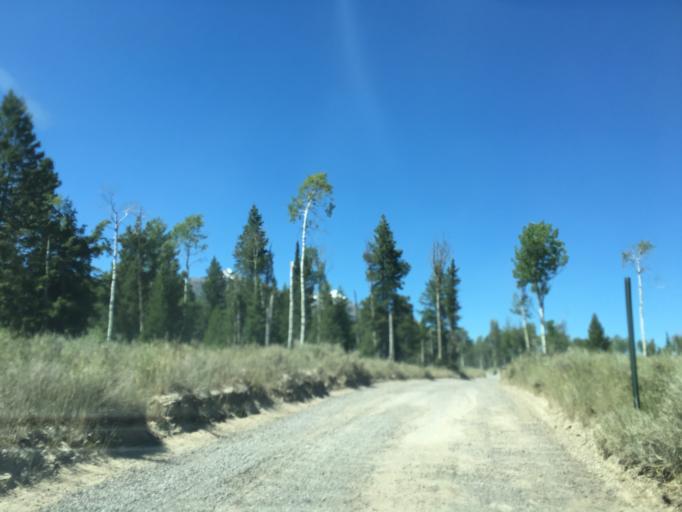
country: US
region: Wyoming
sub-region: Teton County
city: Moose Wilson Road
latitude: 43.6107
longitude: -110.7923
